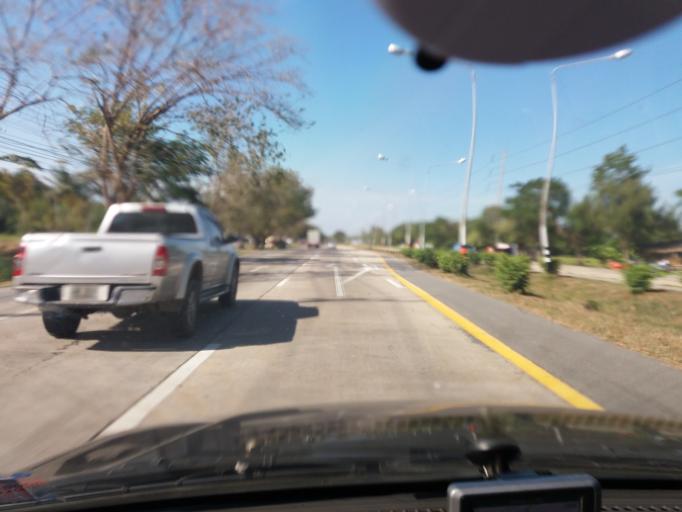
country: TH
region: Suphan Buri
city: Si Prachan
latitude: 14.5807
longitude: 100.1501
